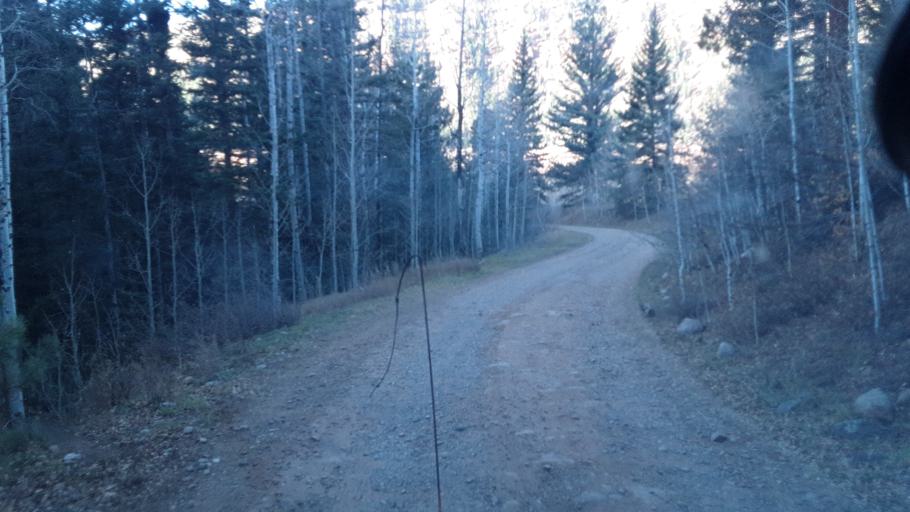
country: US
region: Colorado
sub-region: La Plata County
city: Bayfield
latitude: 37.3952
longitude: -107.6557
